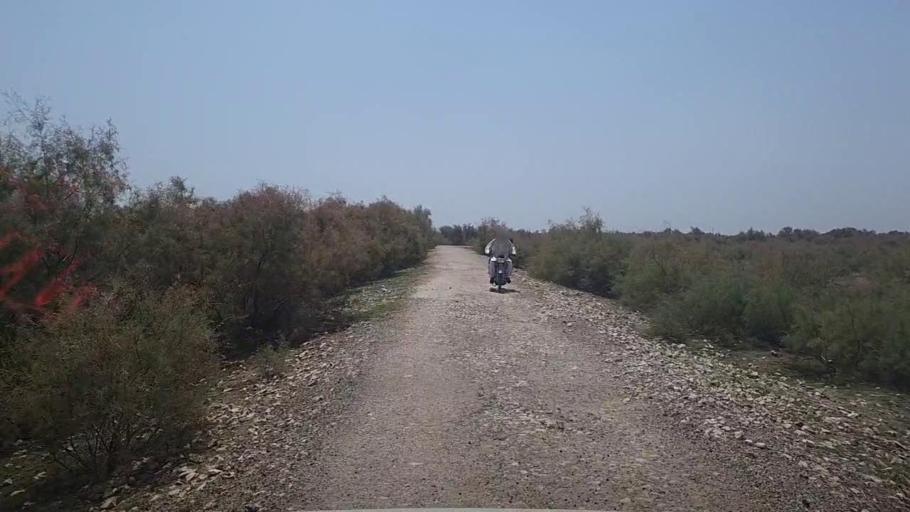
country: PK
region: Sindh
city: Kandhkot
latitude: 28.3038
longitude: 69.3584
